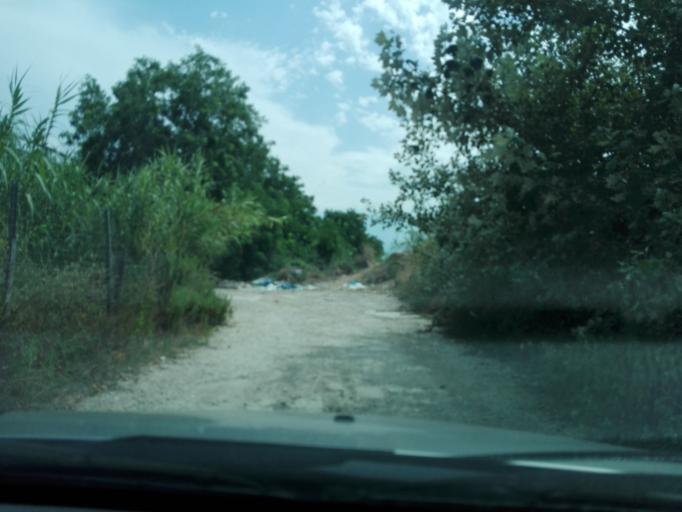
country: IT
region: Abruzzo
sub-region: Provincia di Pescara
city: Cappelle sul Tavo
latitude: 42.4888
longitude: 14.1114
